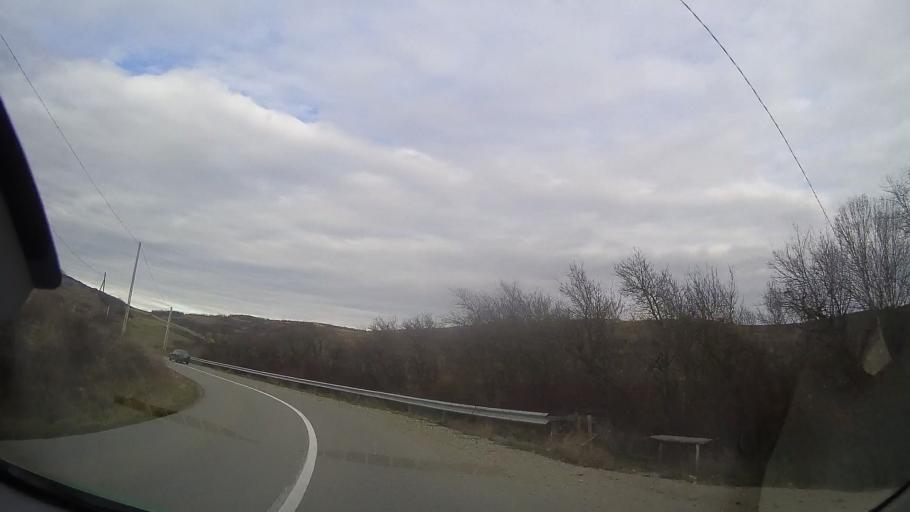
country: RO
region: Bistrita-Nasaud
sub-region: Comuna Milas
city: Milas
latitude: 46.8362
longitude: 24.4484
